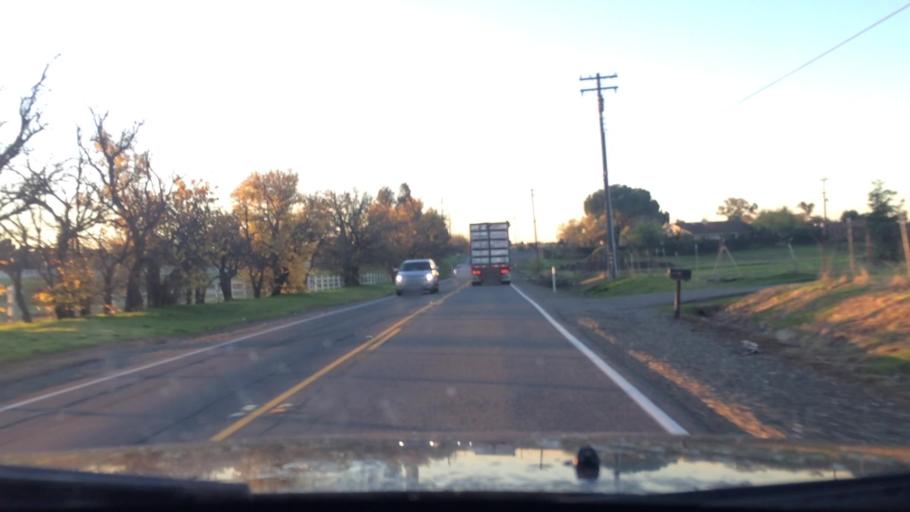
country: US
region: California
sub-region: Sacramento County
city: Vineyard
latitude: 38.5129
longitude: -121.2980
